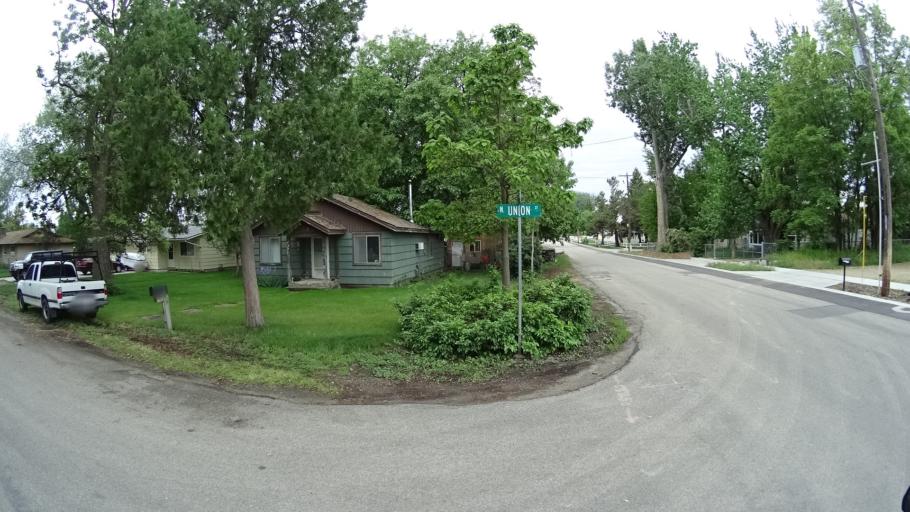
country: US
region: Idaho
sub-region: Ada County
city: Star
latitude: 43.6956
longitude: -116.4955
